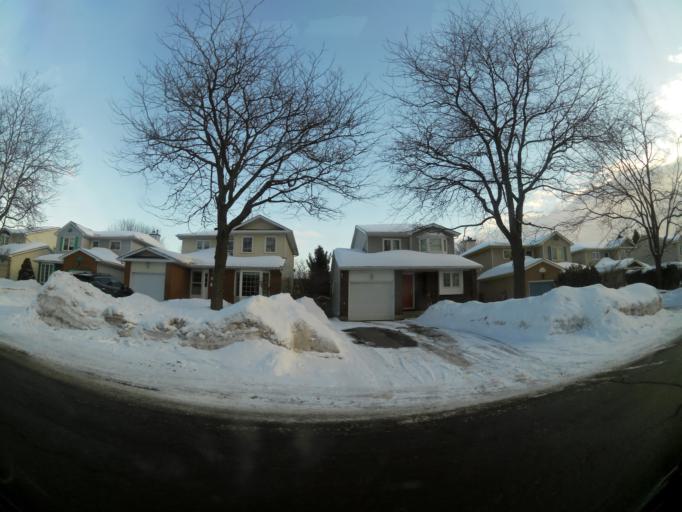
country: CA
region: Ontario
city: Ottawa
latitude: 45.4483
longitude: -75.5387
